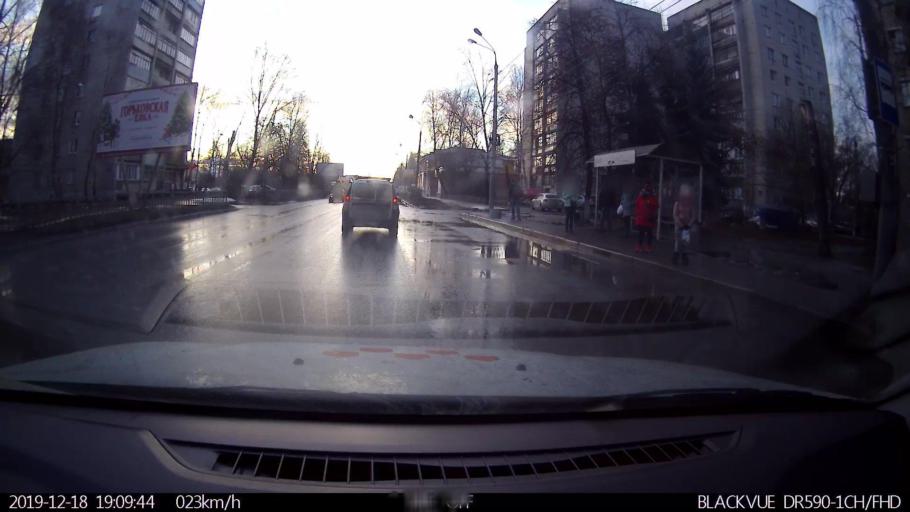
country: RU
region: Nizjnij Novgorod
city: Nizhniy Novgorod
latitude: 56.3175
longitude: 43.8678
